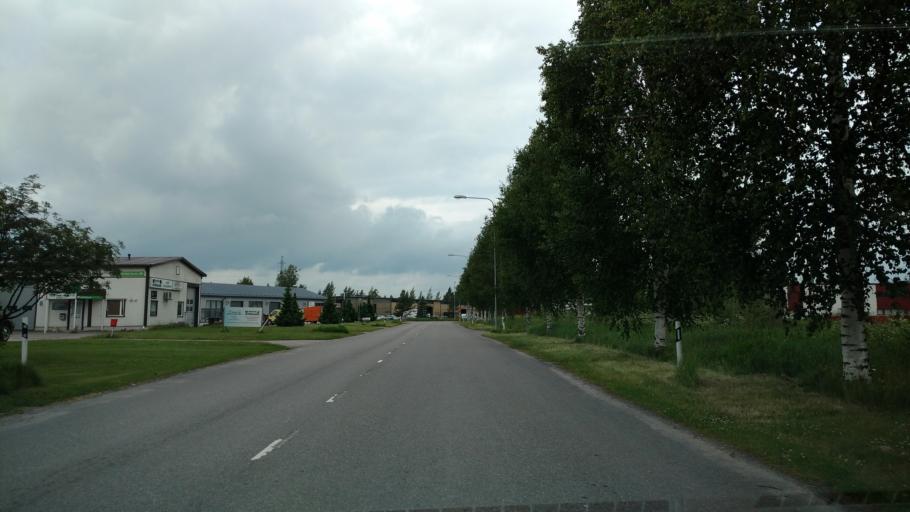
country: FI
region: Varsinais-Suomi
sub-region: Salo
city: Salo
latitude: 60.3805
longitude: 23.1070
